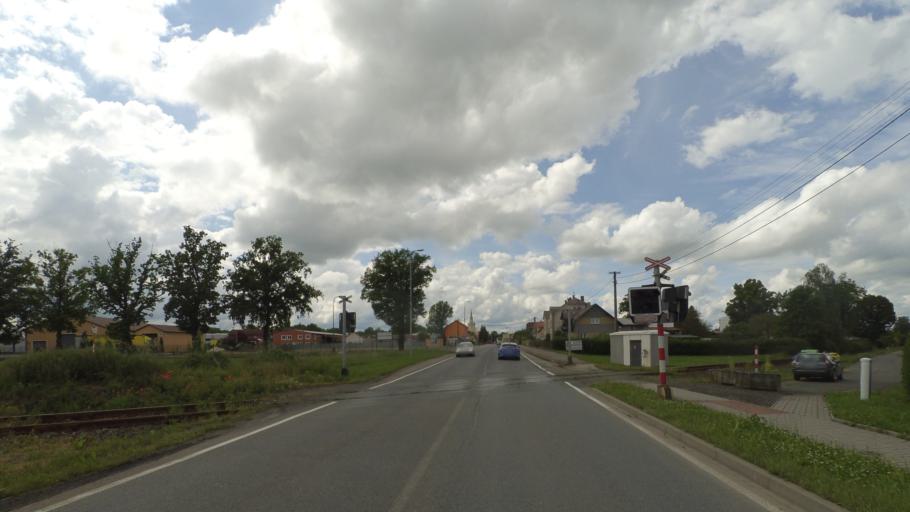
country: CZ
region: Plzensky
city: Bor
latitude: 49.7083
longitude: 12.7848
